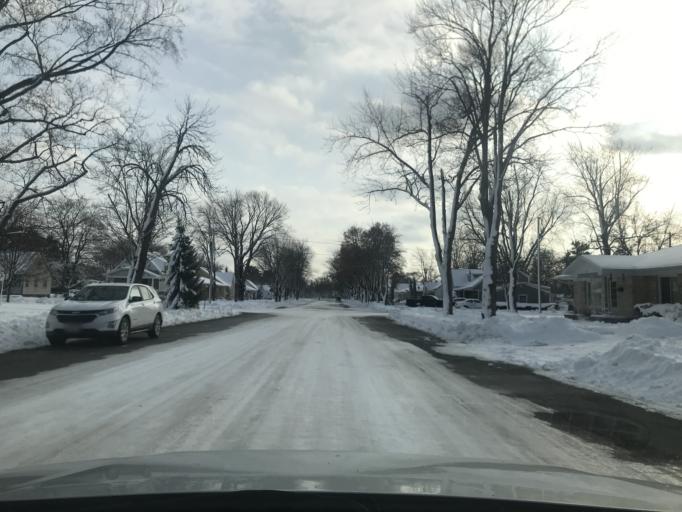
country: US
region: Wisconsin
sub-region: Marinette County
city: Peshtigo
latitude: 45.0533
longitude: -87.7550
